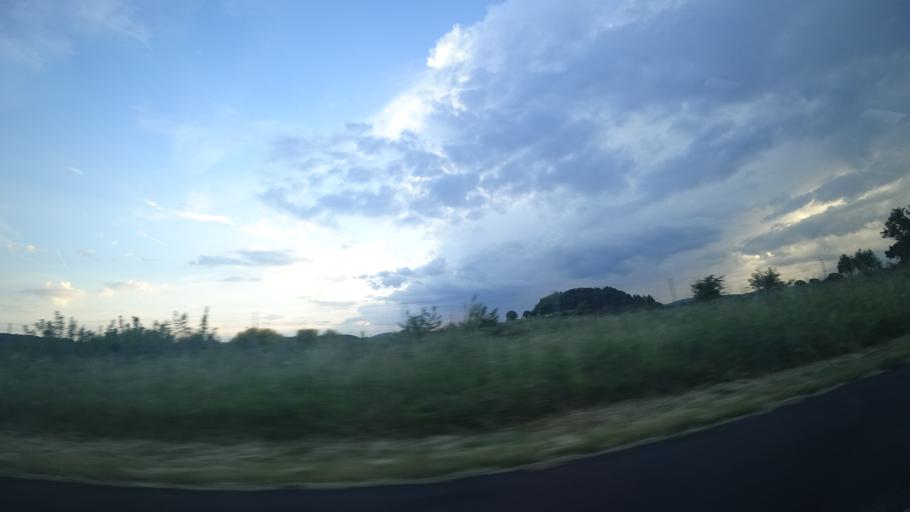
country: FR
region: Languedoc-Roussillon
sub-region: Departement de l'Herault
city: Aspiran
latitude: 43.5922
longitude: 3.4654
